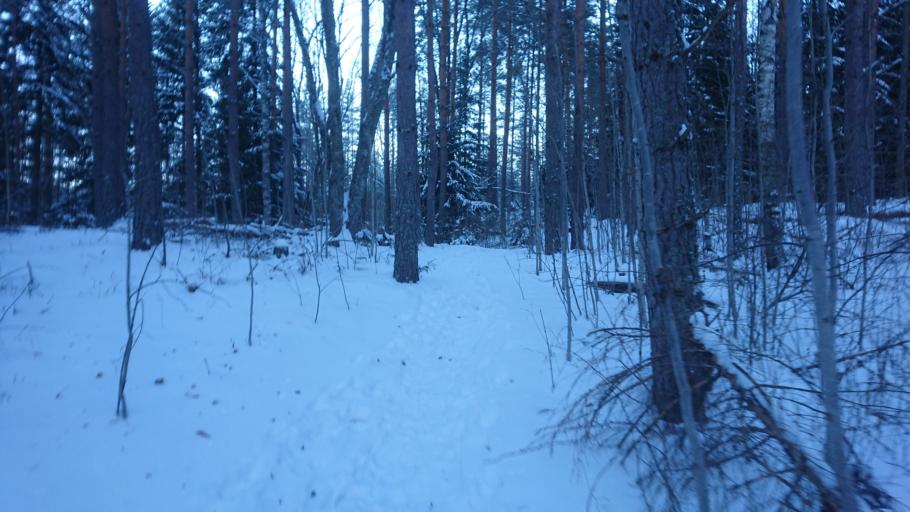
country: SE
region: Uppsala
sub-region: Uppsala Kommun
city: Gamla Uppsala
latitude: 59.9545
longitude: 17.5916
